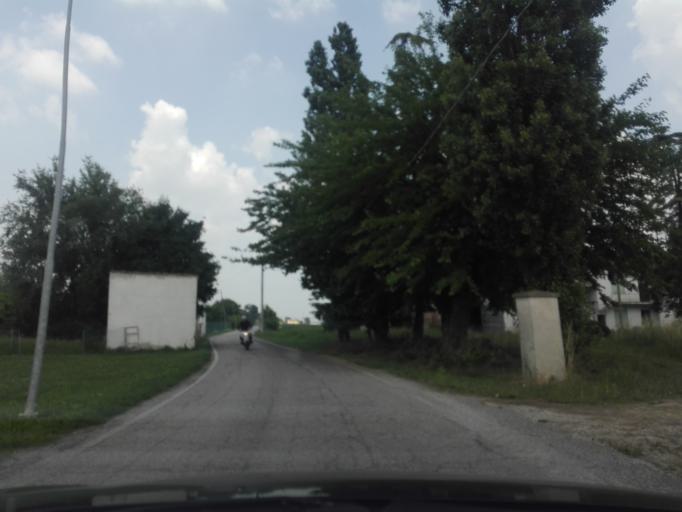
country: IT
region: Veneto
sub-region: Provincia di Rovigo
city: Crespino
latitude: 44.9960
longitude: 11.9002
